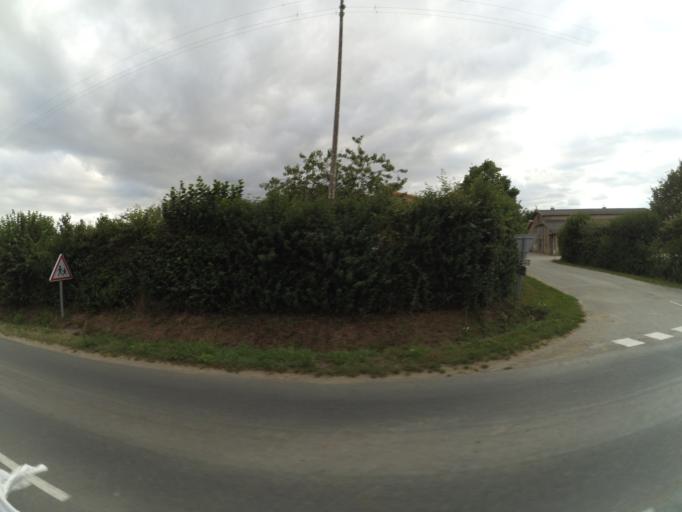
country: FR
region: Pays de la Loire
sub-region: Departement de la Vendee
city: Saint-Andre-Treize-Voies
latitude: 46.9314
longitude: -1.4028
